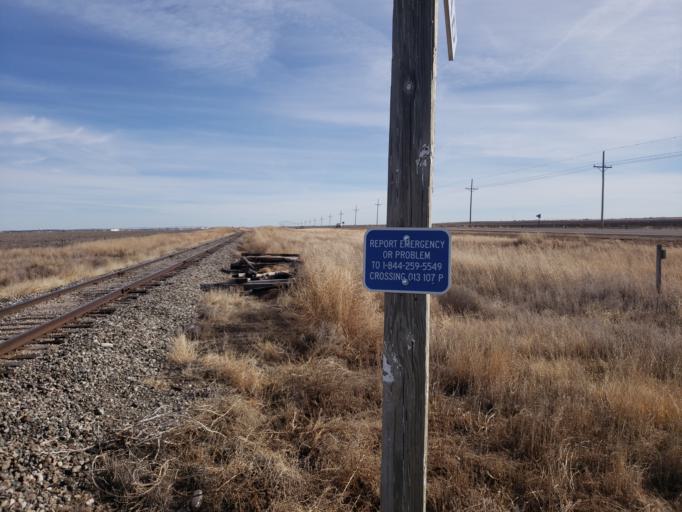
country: US
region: Kansas
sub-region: Ford County
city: Dodge City
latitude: 37.7137
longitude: -100.1060
